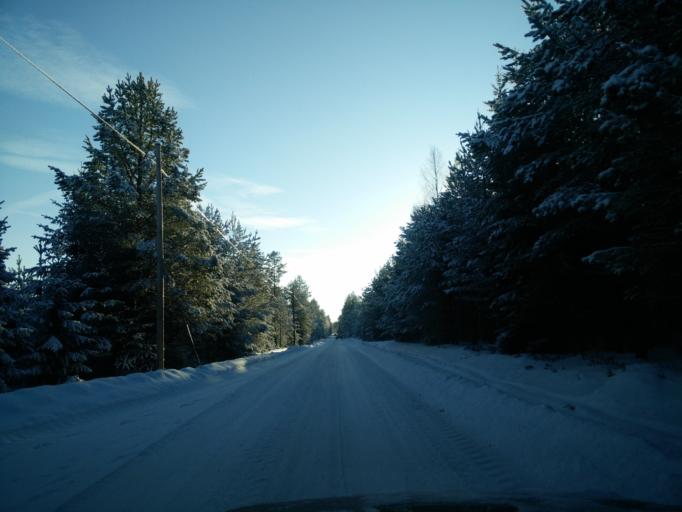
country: SE
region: Vaesternorrland
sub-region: Sundsvalls Kommun
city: Njurundabommen
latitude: 62.2164
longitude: 17.4935
